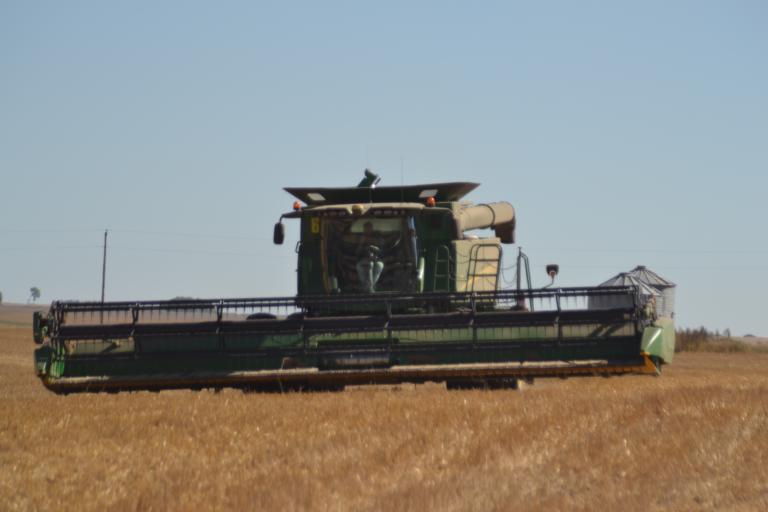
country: US
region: North Dakota
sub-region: McLean County
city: Garrison
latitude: 47.7369
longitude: -101.8079
